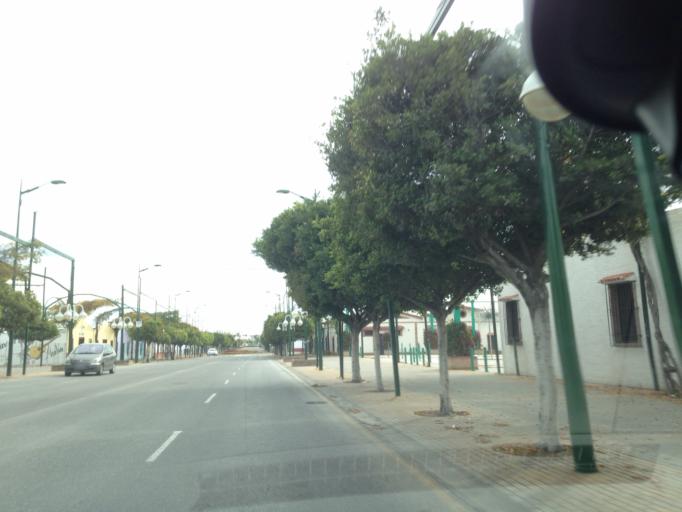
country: ES
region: Andalusia
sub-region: Provincia de Malaga
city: Malaga
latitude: 36.7047
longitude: -4.4641
